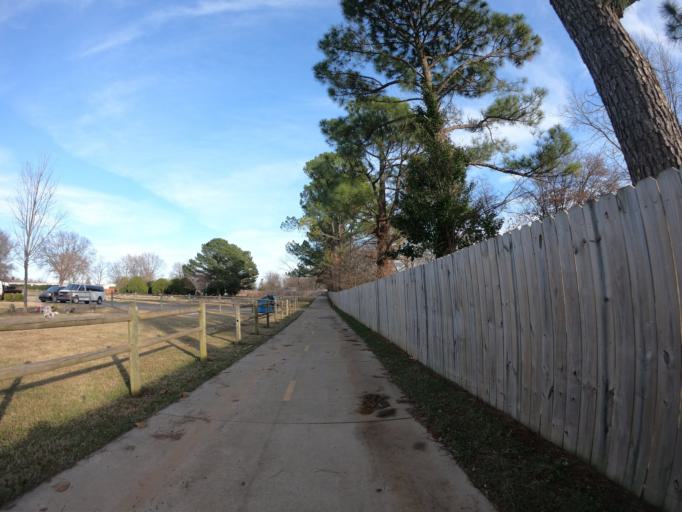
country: US
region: Arkansas
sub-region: Benton County
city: Rogers
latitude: 36.3328
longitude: -94.1725
